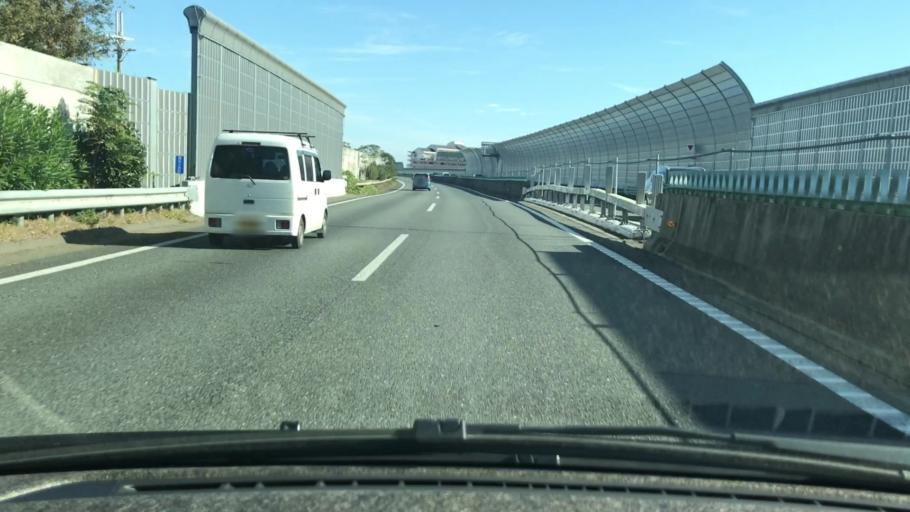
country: JP
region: Osaka
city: Toyonaka
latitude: 34.7455
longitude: 135.4494
